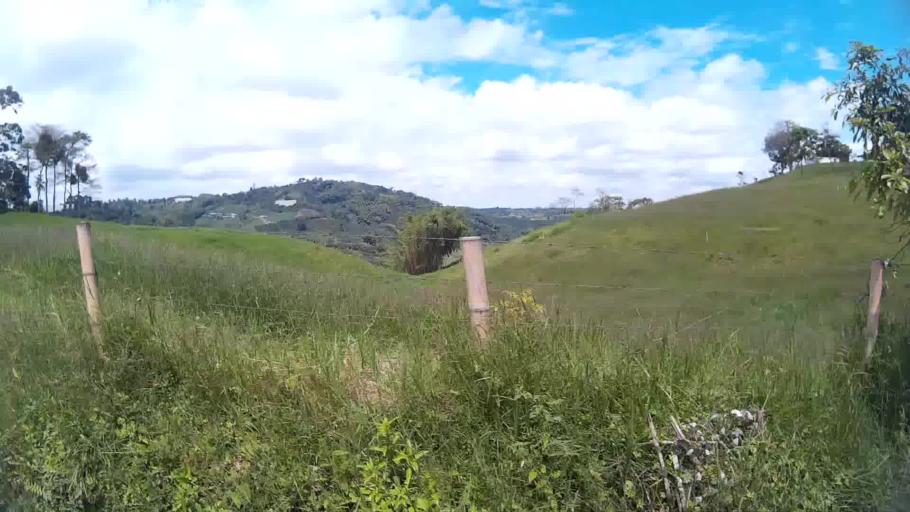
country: CO
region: Valle del Cauca
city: Ulloa
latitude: 4.7208
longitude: -75.7073
